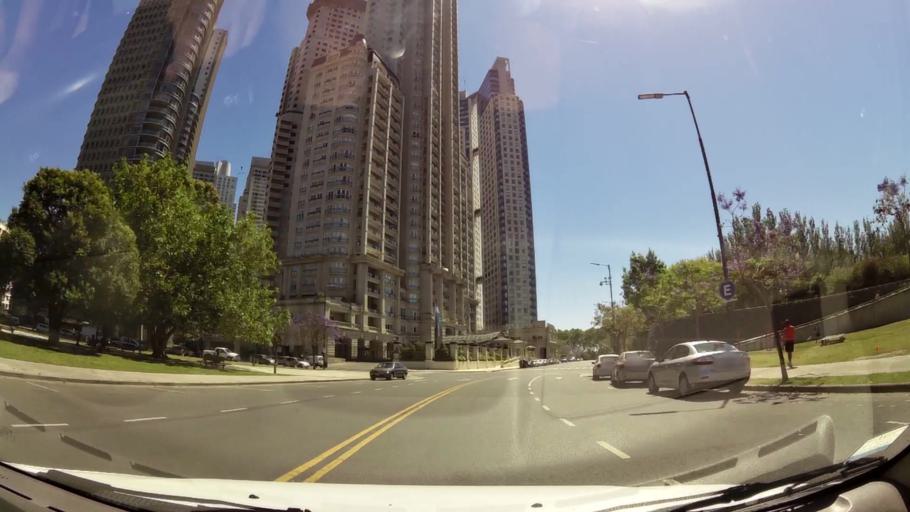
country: AR
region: Buenos Aires F.D.
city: Buenos Aires
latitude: -34.6141
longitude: -58.3606
